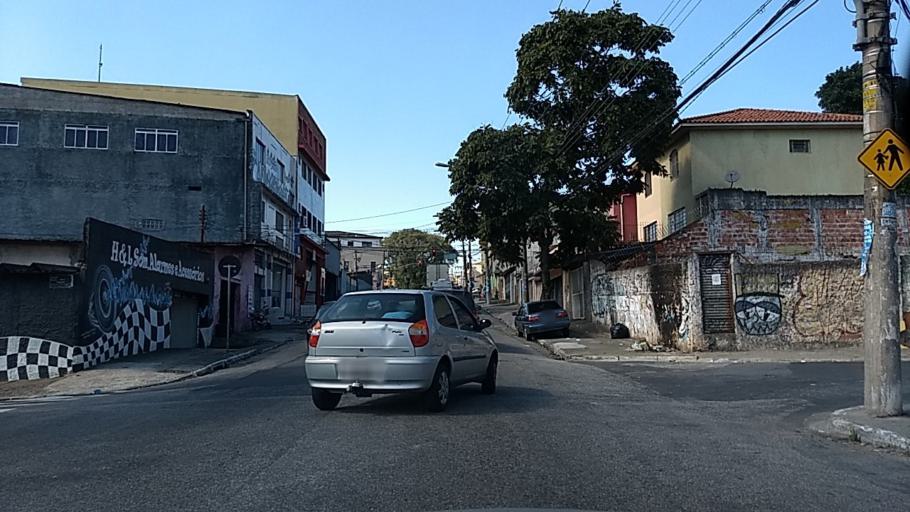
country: BR
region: Sao Paulo
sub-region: Guarulhos
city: Guarulhos
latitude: -23.4821
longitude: -46.5905
